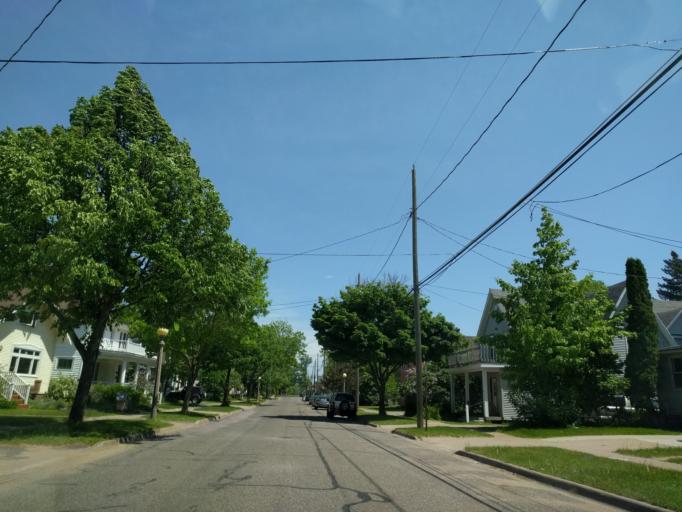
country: US
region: Michigan
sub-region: Marquette County
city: Marquette
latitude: 46.5462
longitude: -87.3938
